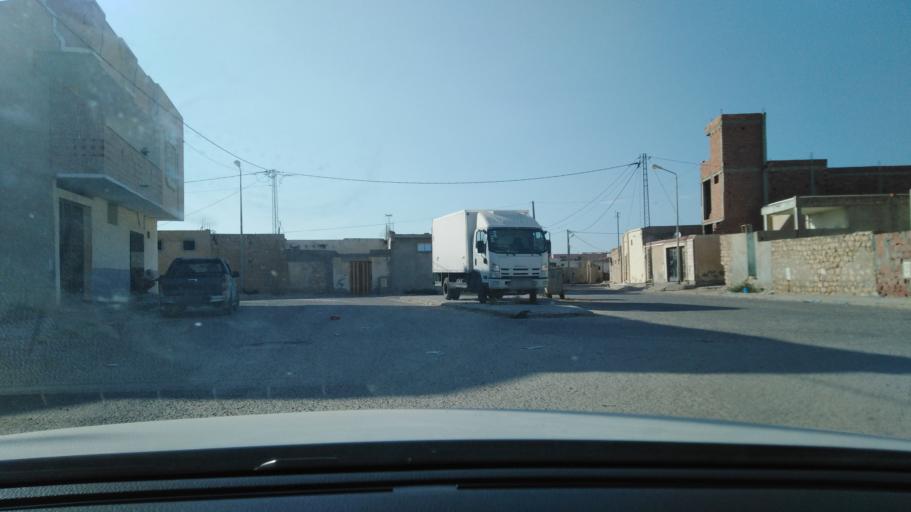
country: TN
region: Qabis
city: Gabes
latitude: 33.9364
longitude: 10.0701
